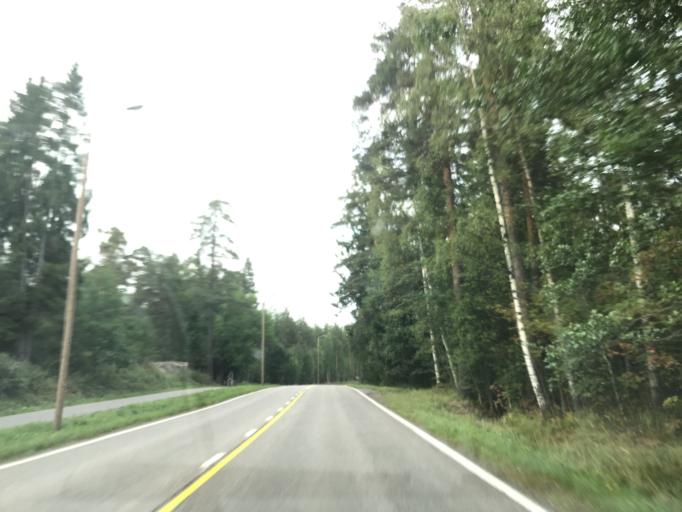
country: FI
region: Uusimaa
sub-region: Helsinki
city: Kirkkonummi
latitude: 60.2599
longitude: 24.4478
